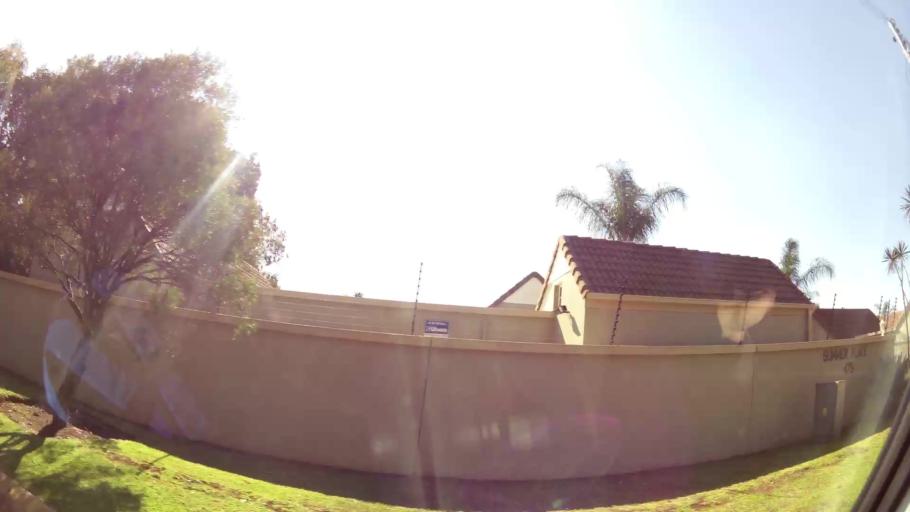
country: ZA
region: Gauteng
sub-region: City of Tshwane Metropolitan Municipality
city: Pretoria
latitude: -25.7681
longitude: 28.2721
